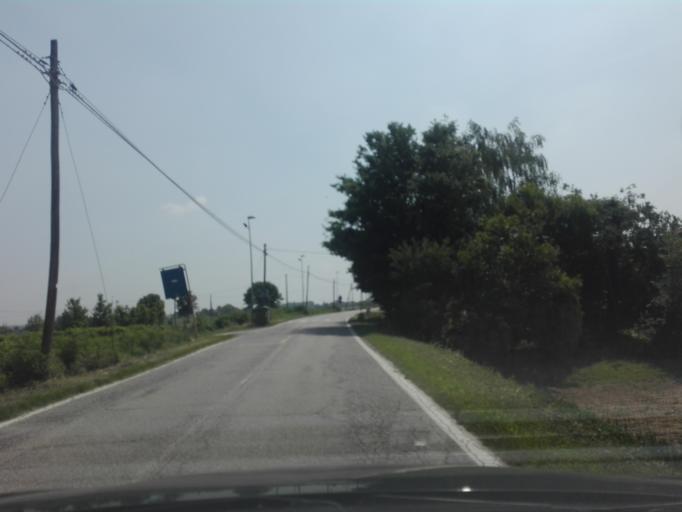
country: IT
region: Veneto
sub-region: Provincia di Rovigo
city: Lama Pezzoli
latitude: 45.0456
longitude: 11.8895
